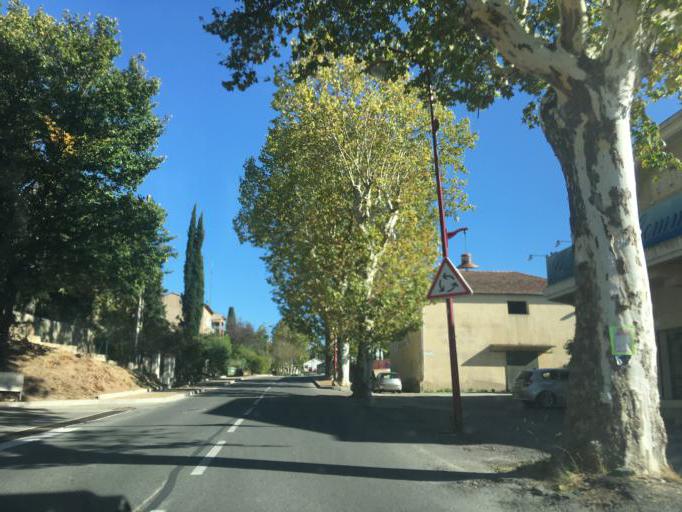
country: FR
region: Provence-Alpes-Cote d'Azur
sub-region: Departement du Var
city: Salernes
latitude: 43.5618
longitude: 6.2372
